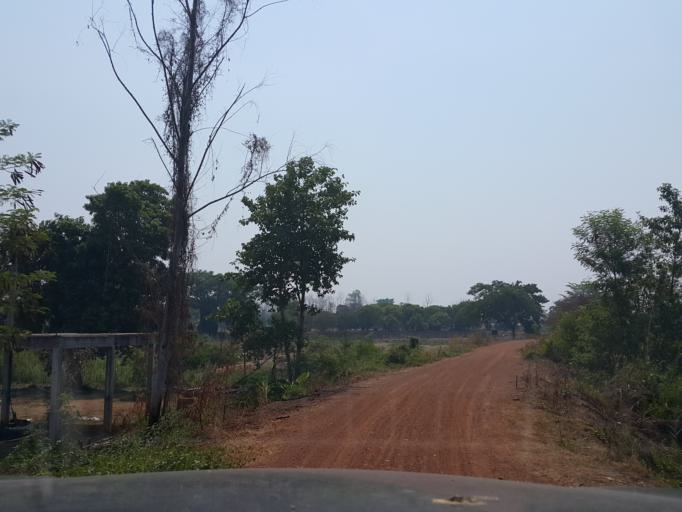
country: TH
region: Sukhothai
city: Thung Saliam
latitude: 17.3152
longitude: 99.5604
